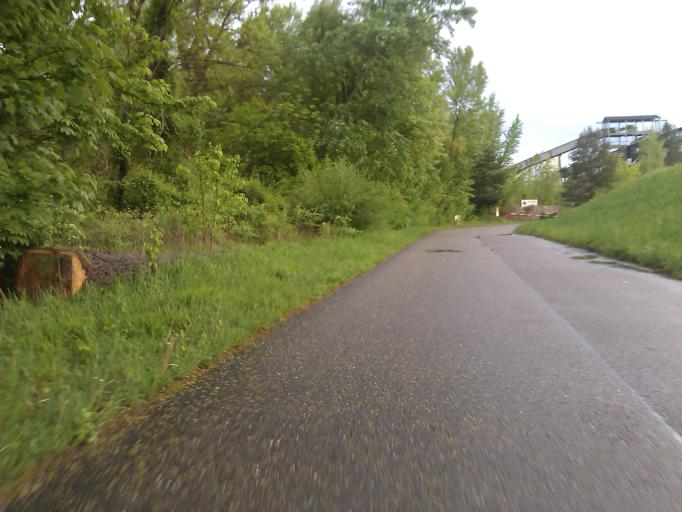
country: FR
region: Alsace
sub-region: Departement du Bas-Rhin
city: Drusenheim
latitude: 48.7438
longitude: 7.9711
